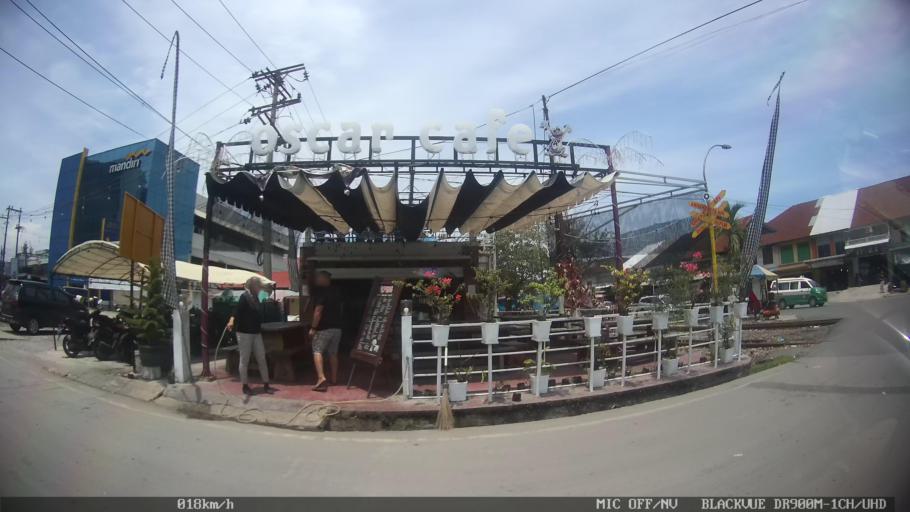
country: ID
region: North Sumatra
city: Belawan
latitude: 3.7826
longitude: 98.6882
